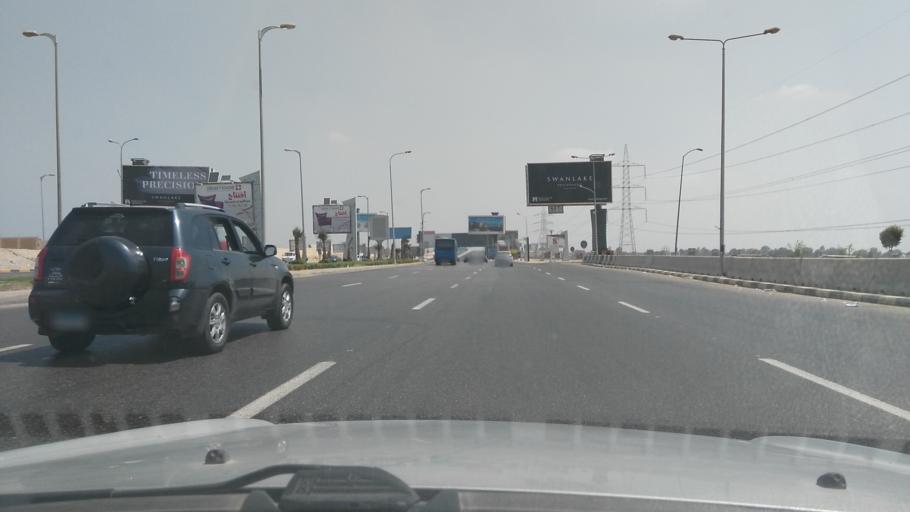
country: EG
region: Al Jizah
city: Awsim
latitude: 30.0428
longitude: 31.0456
